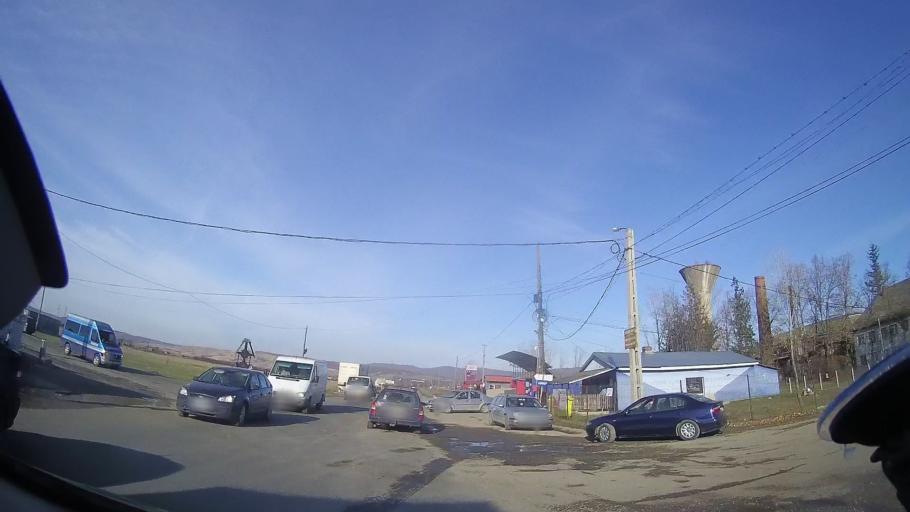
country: RO
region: Bihor
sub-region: Comuna Astileu
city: Astileu
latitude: 47.0375
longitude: 22.3916
